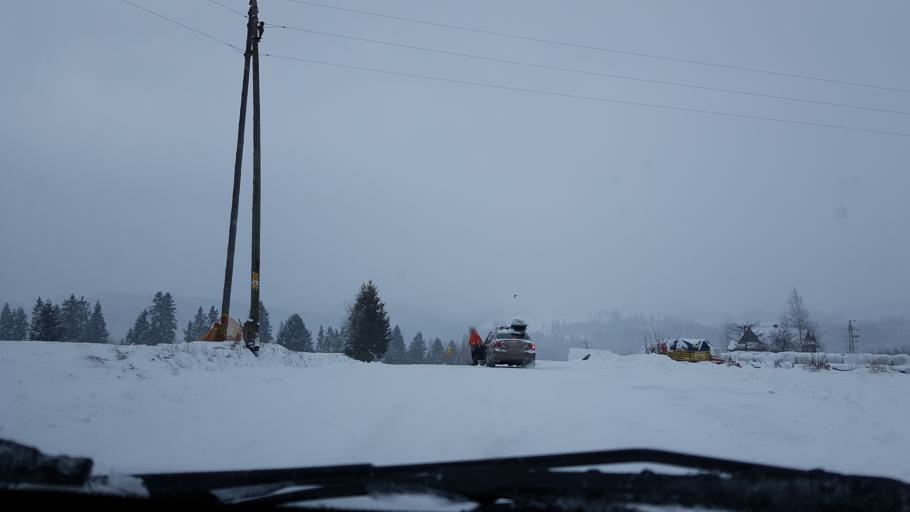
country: PL
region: Lesser Poland Voivodeship
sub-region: Powiat tatrzanski
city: Czarna Gora
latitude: 49.3525
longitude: 20.1460
